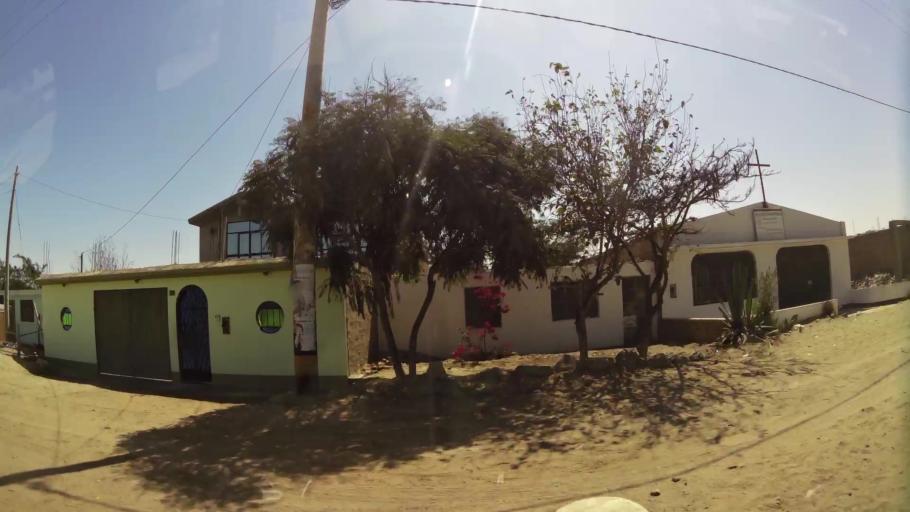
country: PE
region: Ica
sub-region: Provincia de Ica
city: Subtanjalla
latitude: -14.0358
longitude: -75.7513
